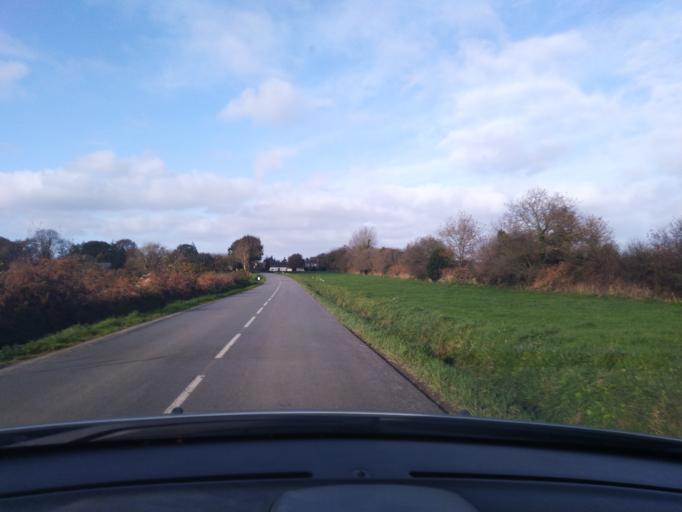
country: FR
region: Brittany
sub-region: Departement du Finistere
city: Plouigneau
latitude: 48.5457
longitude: -3.6833
